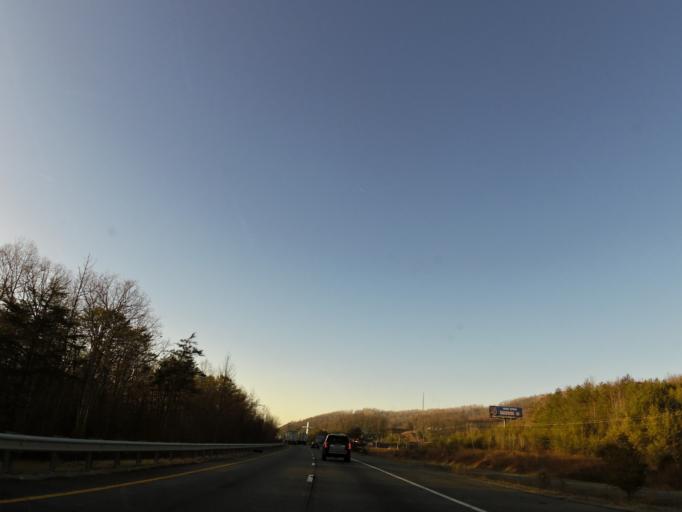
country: US
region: Tennessee
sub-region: Campbell County
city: Jacksboro
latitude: 36.3682
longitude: -84.2340
